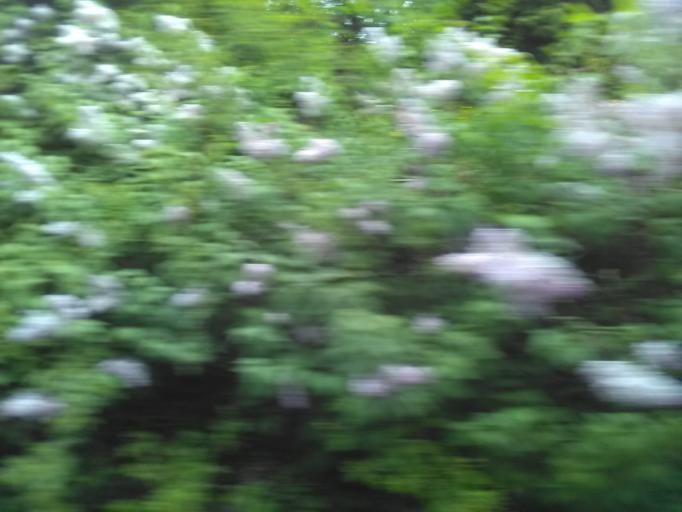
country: DE
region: Bavaria
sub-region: Regierungsbezirk Mittelfranken
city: Heroldsberg
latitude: 49.5329
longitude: 11.1489
